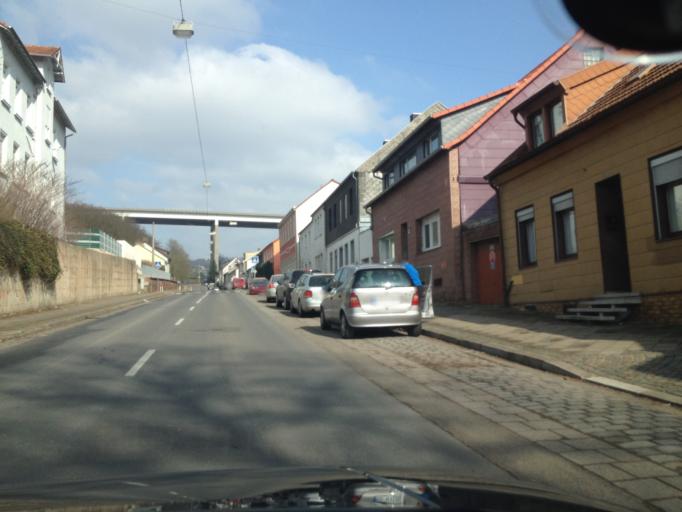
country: DE
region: Saarland
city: Friedrichsthal
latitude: 49.3127
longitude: 7.0835
